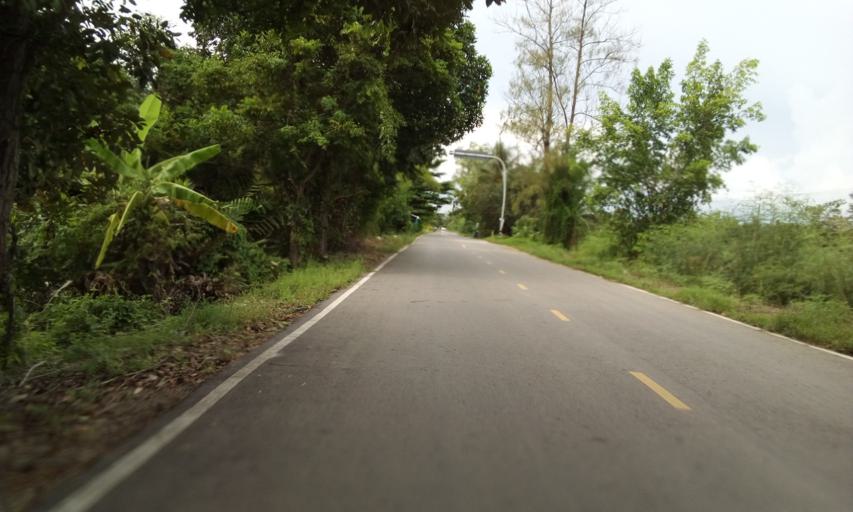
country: TH
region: Pathum Thani
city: Nong Suea
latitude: 14.1602
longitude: 100.8232
